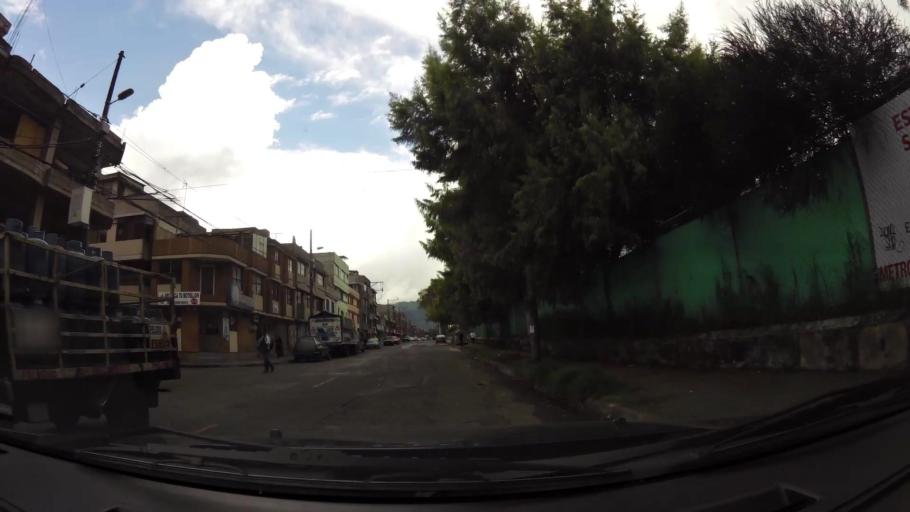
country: EC
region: Pichincha
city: Quito
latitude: -0.2663
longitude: -78.5359
